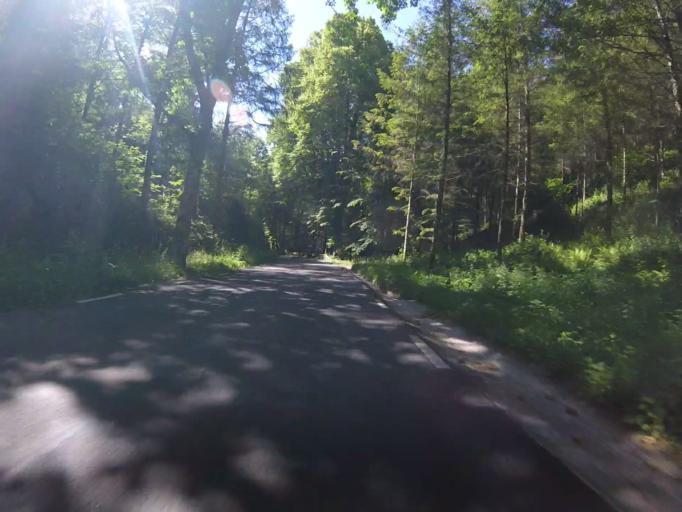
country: ES
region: Basque Country
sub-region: Provincia de Guipuzcoa
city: Albiztur
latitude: 43.1198
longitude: -2.1610
